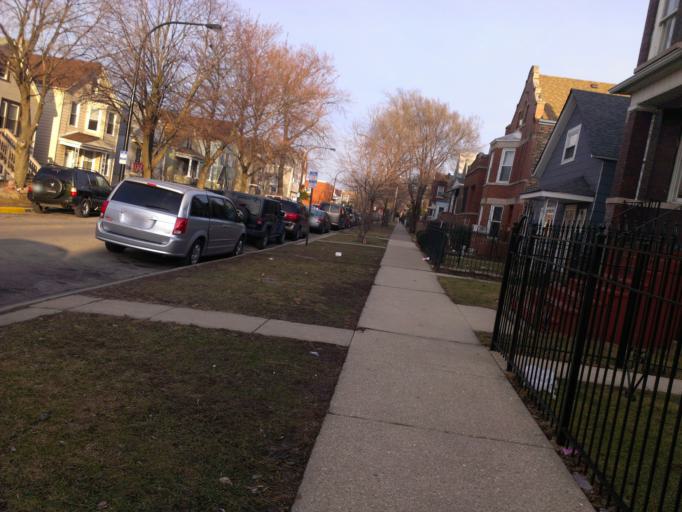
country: US
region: Illinois
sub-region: Cook County
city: Cicero
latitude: 41.8492
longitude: -87.7604
